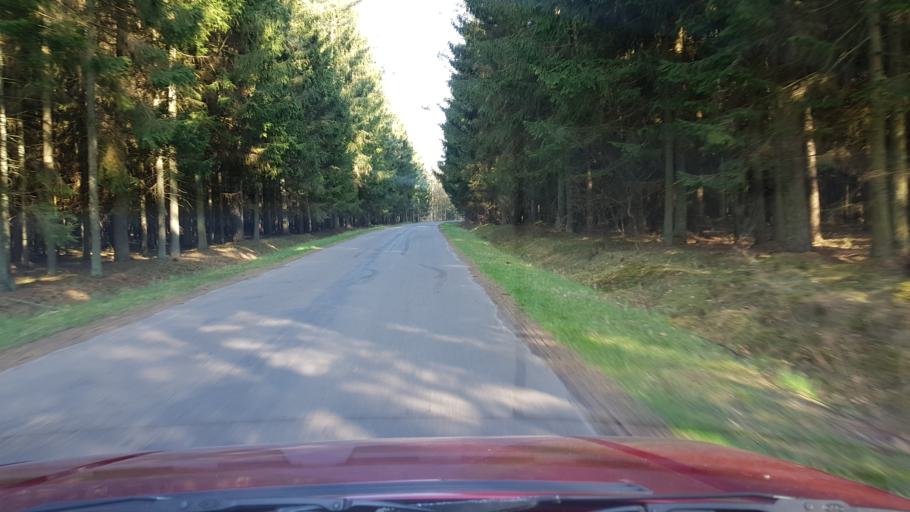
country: PL
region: West Pomeranian Voivodeship
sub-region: Powiat gryficki
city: Ploty
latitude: 53.8331
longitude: 15.3063
